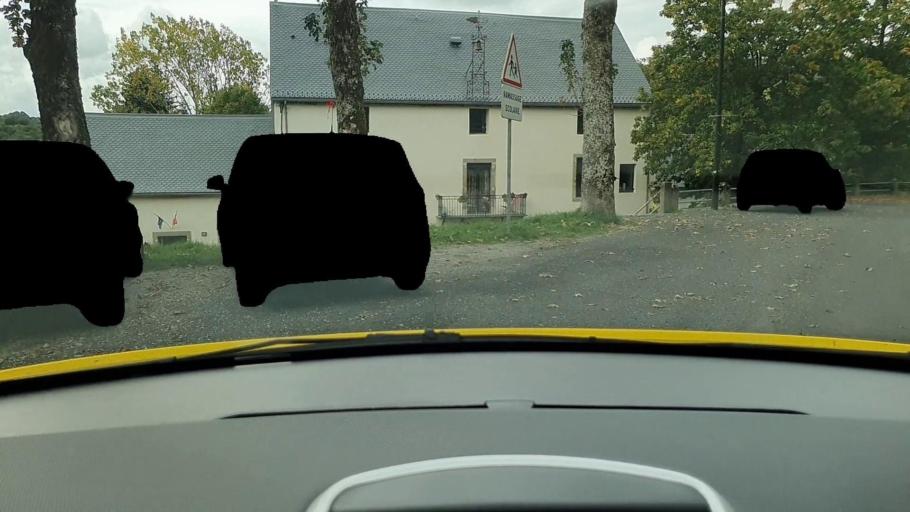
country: FR
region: Languedoc-Roussillon
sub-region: Departement de la Lozere
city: Meyrueis
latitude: 44.0644
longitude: 3.4450
